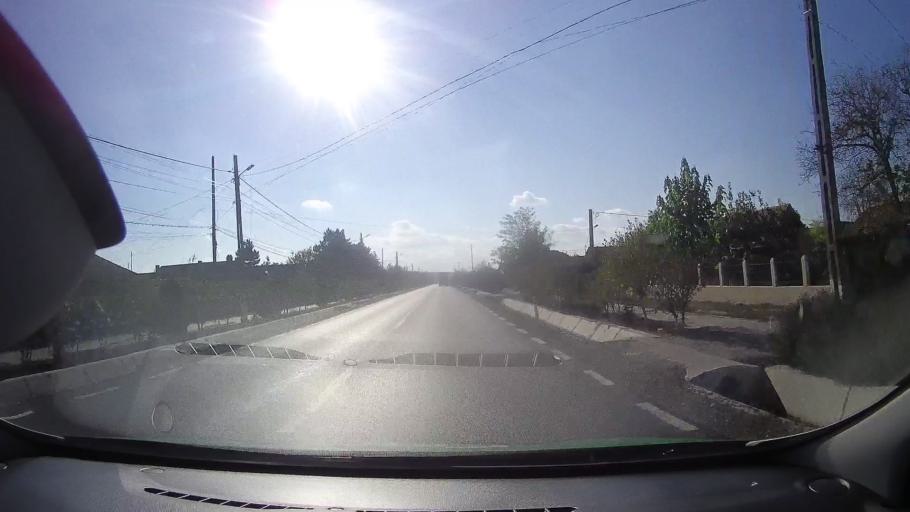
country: RO
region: Tulcea
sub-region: Comuna Baia
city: Baia
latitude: 44.7303
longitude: 28.6815
